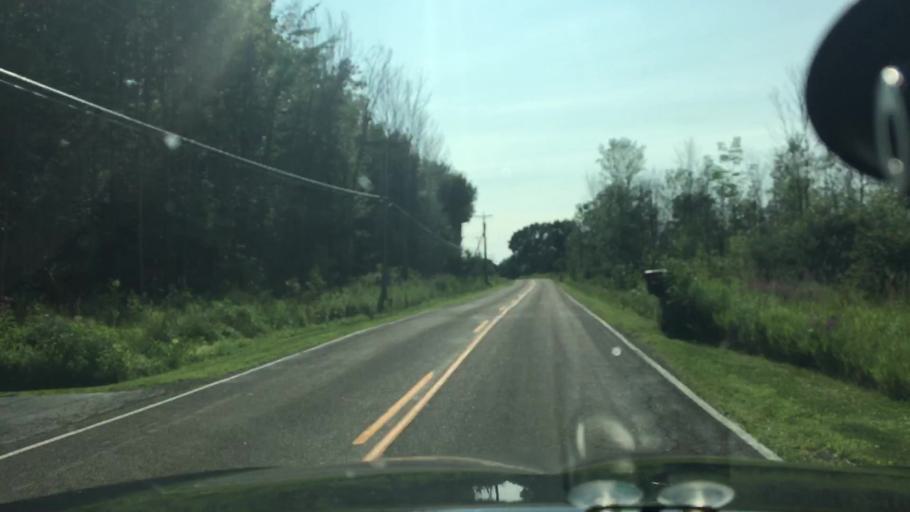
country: US
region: New York
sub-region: Erie County
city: Angola
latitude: 42.6296
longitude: -78.9853
